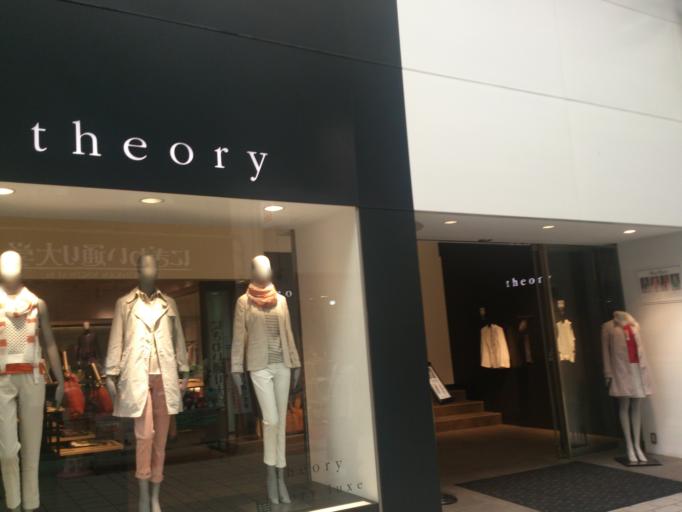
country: JP
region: Kagoshima
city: Kagoshima-shi
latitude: 31.5910
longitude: 130.5542
